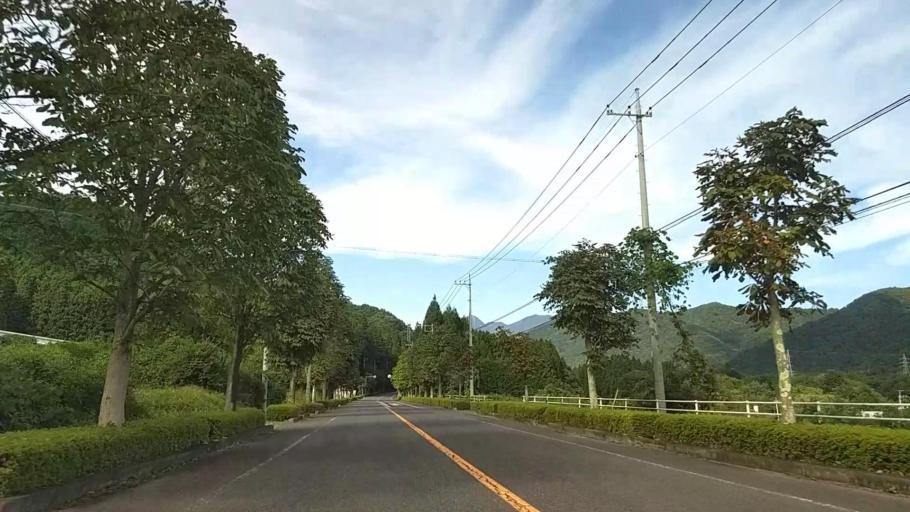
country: JP
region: Tochigi
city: Imaichi
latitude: 36.8056
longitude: 139.7032
